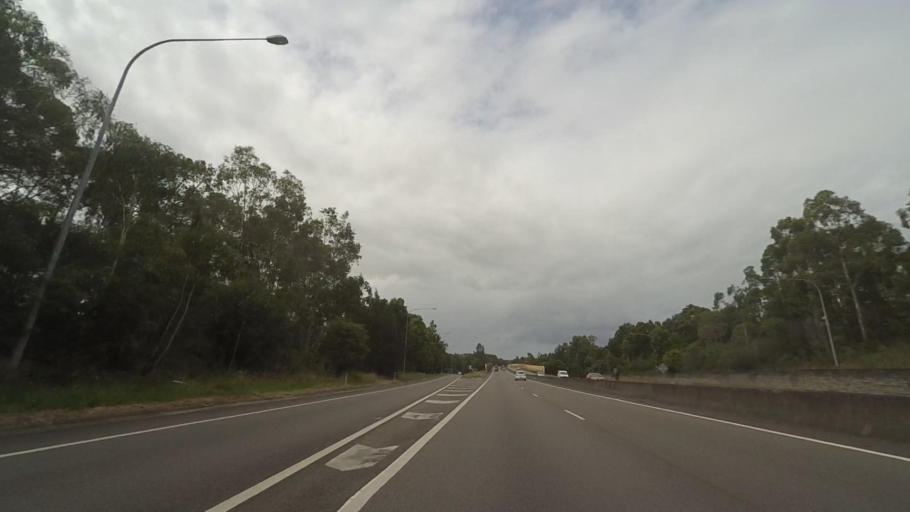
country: AU
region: New South Wales
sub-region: Port Stephens Shire
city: Raymond Terrace
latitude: -32.7591
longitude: 151.7647
